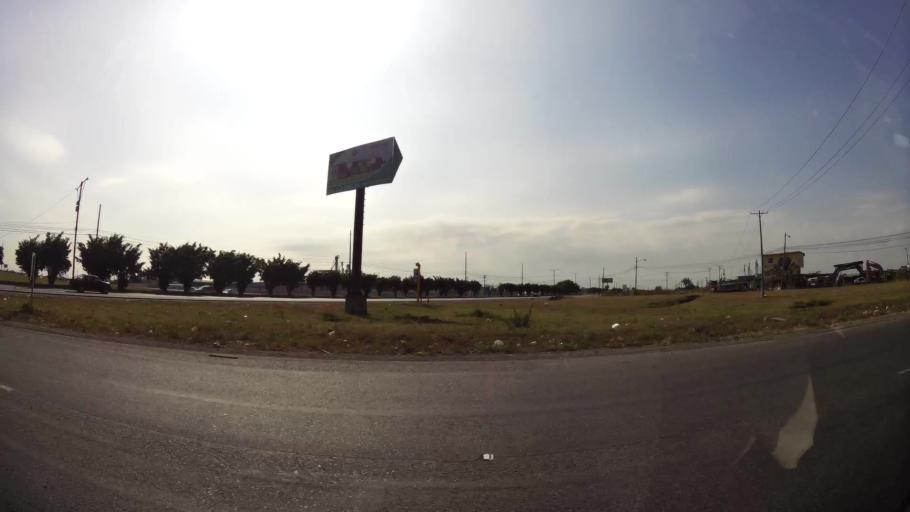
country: EC
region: Guayas
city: Eloy Alfaro
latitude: -2.1858
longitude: -79.8099
